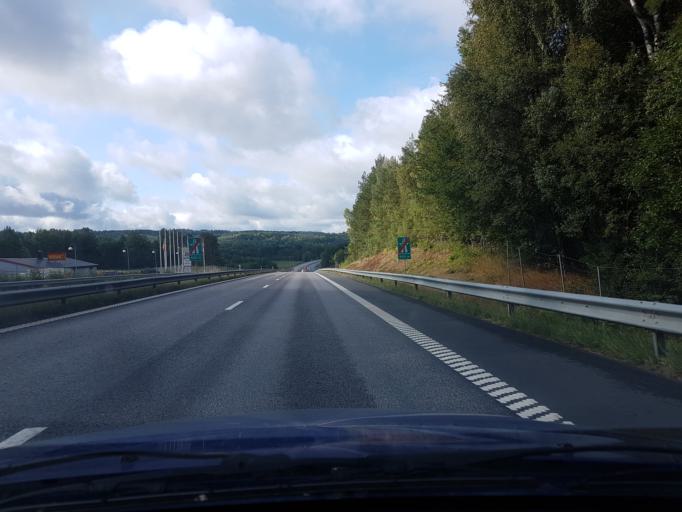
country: SE
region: Vaestra Goetaland
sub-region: Alingsas Kommun
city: Ingared
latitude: 57.8520
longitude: 12.4728
